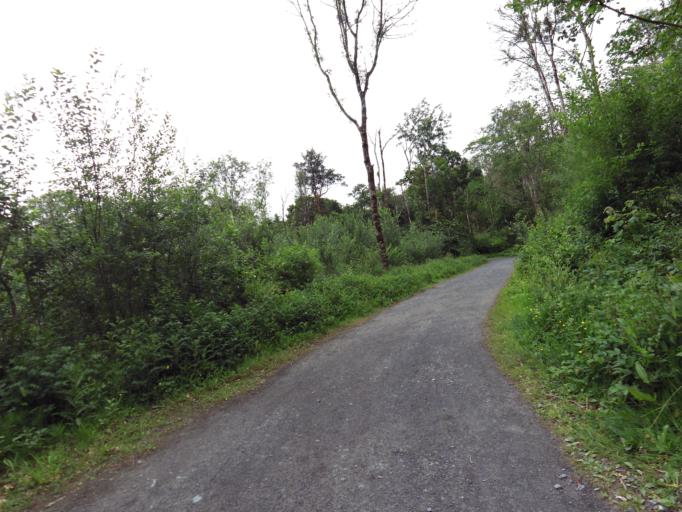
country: IE
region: Connaught
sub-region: County Galway
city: Gort
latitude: 53.0829
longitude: -8.8449
